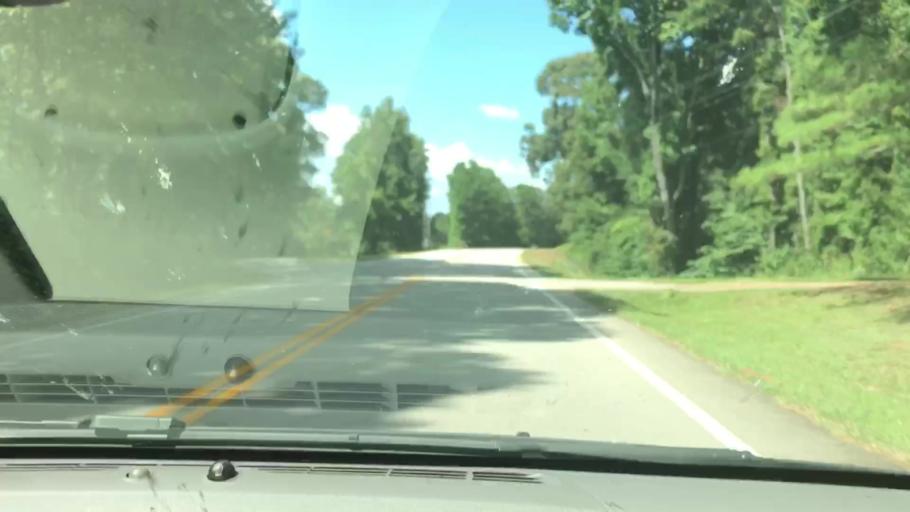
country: US
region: Georgia
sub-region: Troup County
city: La Grange
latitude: 33.1189
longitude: -85.0888
